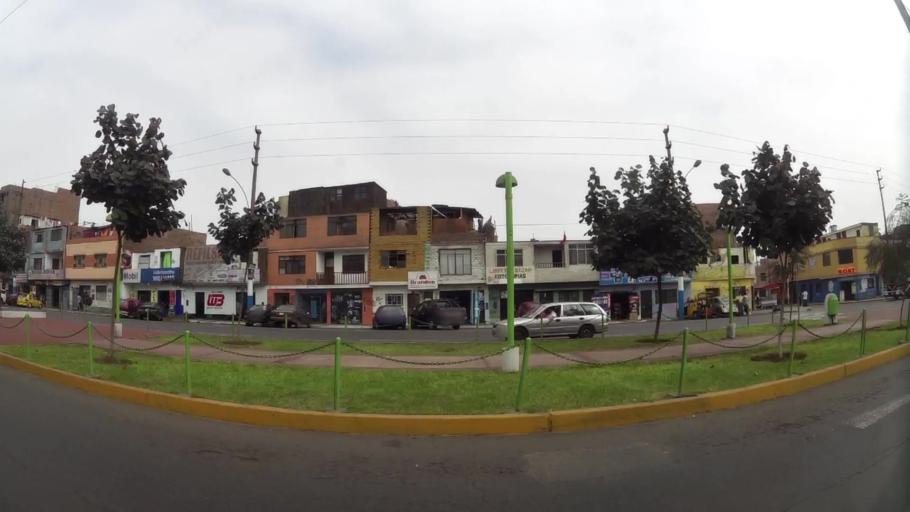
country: PE
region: Callao
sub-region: Callao
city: Callao
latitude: -12.0301
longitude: -77.0923
